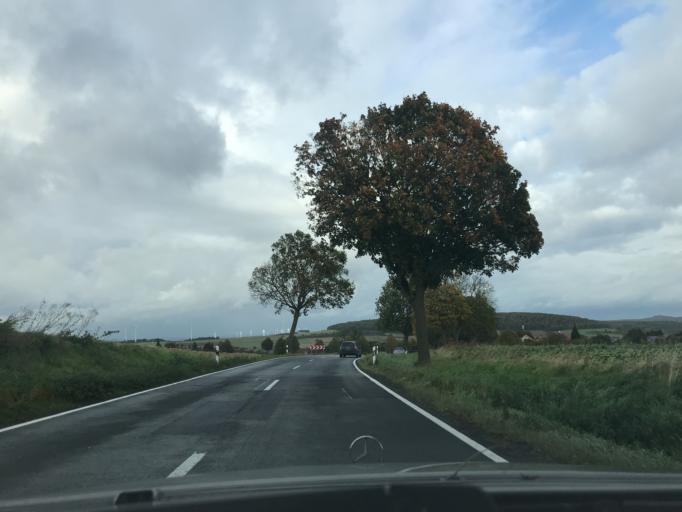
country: DE
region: Hesse
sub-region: Regierungsbezirk Kassel
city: Breuna
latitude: 51.4376
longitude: 9.2341
